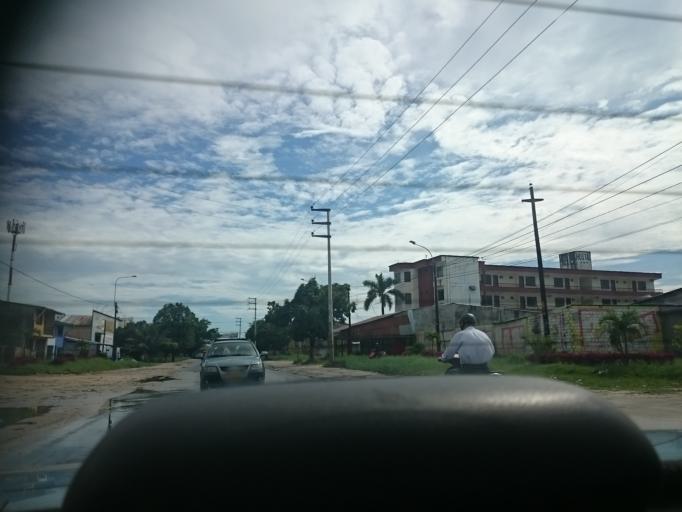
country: PE
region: Loreto
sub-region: Provincia de Maynas
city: Iquitos
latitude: -3.7875
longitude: -73.2998
